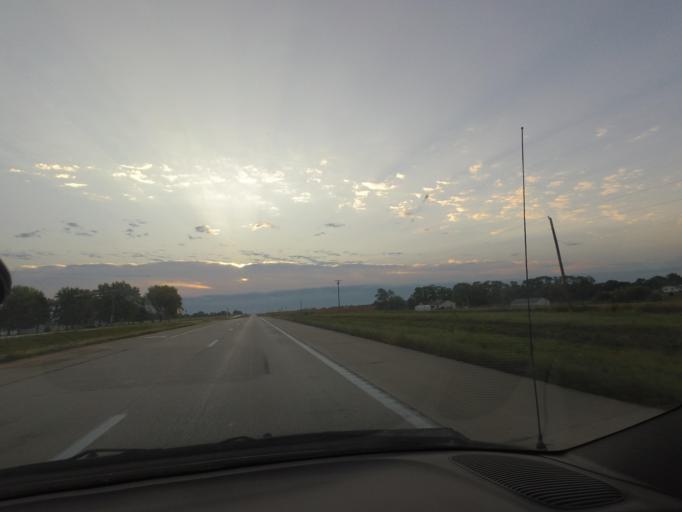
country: US
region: Missouri
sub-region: Macon County
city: Macon
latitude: 39.7503
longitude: -92.3612
